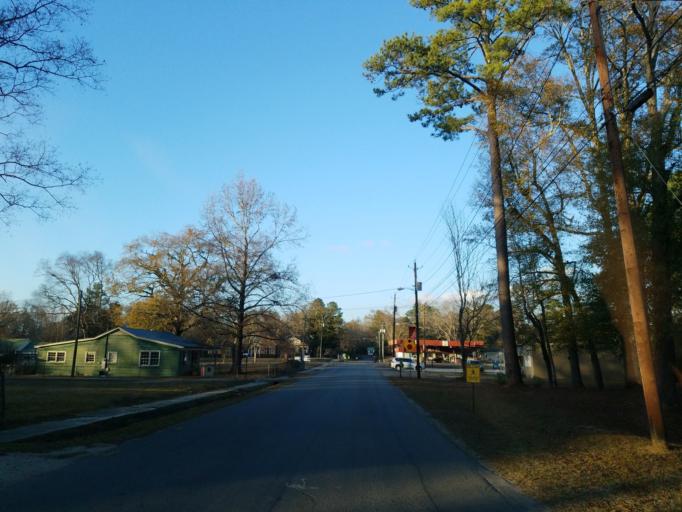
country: US
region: Mississippi
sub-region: Clarke County
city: Stonewall
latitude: 32.1747
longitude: -88.8212
